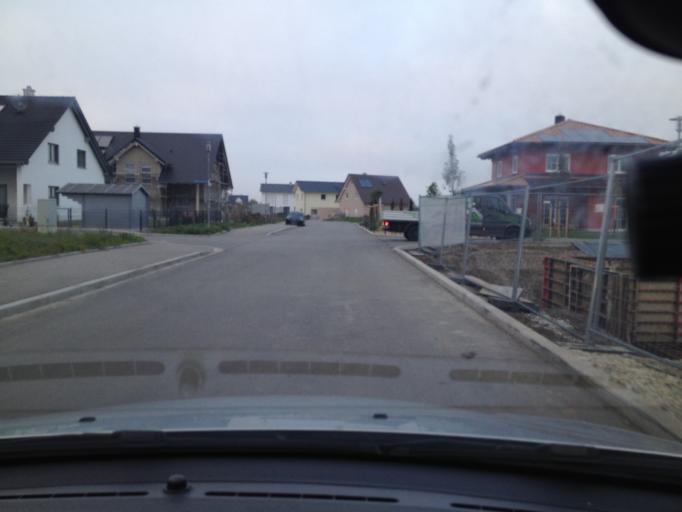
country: DE
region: Bavaria
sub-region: Swabia
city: Kleinaitingen
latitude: 48.2179
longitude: 10.8463
